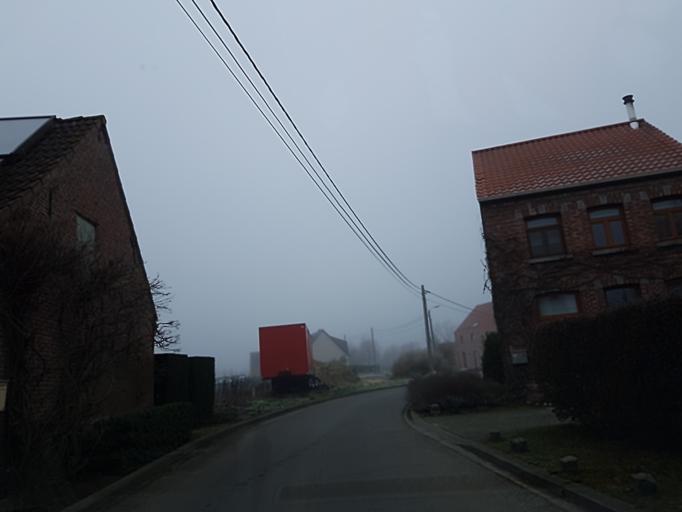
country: BE
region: Flanders
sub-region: Provincie Vlaams-Brabant
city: Zemst
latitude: 50.9934
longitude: 4.4275
